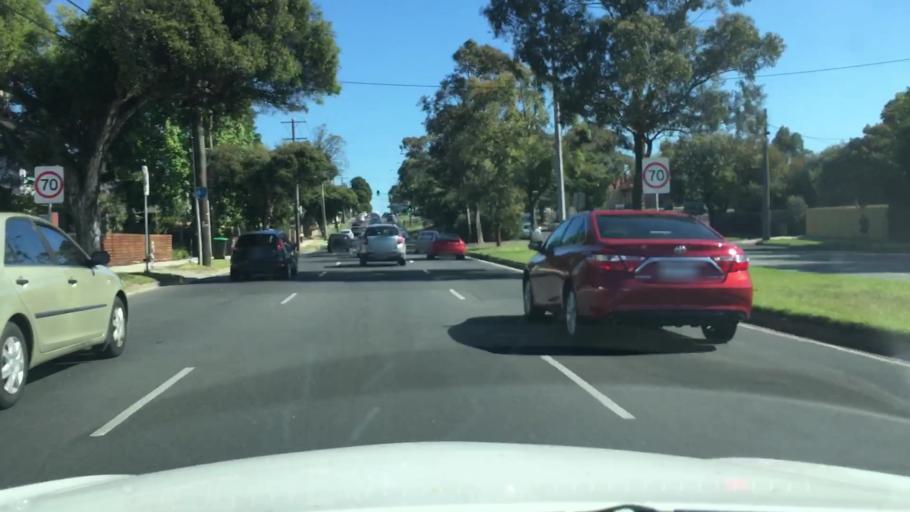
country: AU
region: Victoria
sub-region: Whitehorse
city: Nunawading
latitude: -37.8135
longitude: 145.1769
